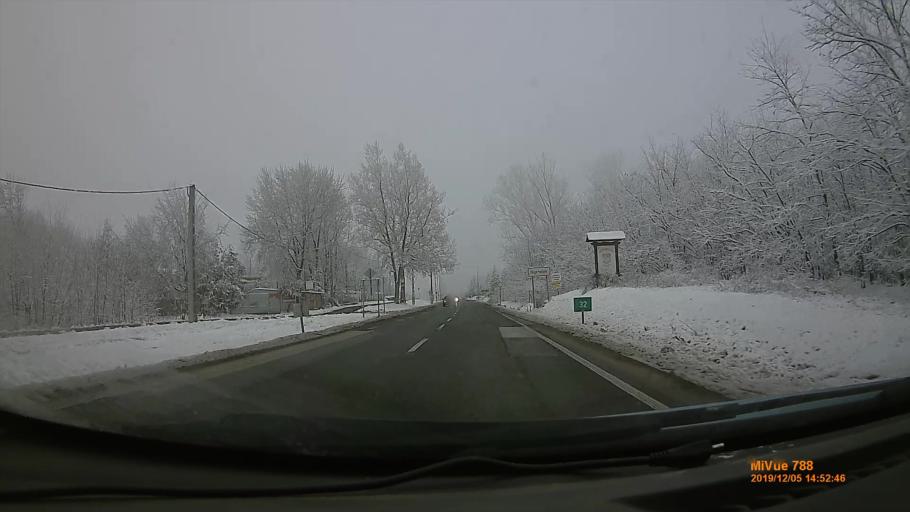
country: HU
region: Szabolcs-Szatmar-Bereg
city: Nyirtelek
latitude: 48.0044
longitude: 21.6405
